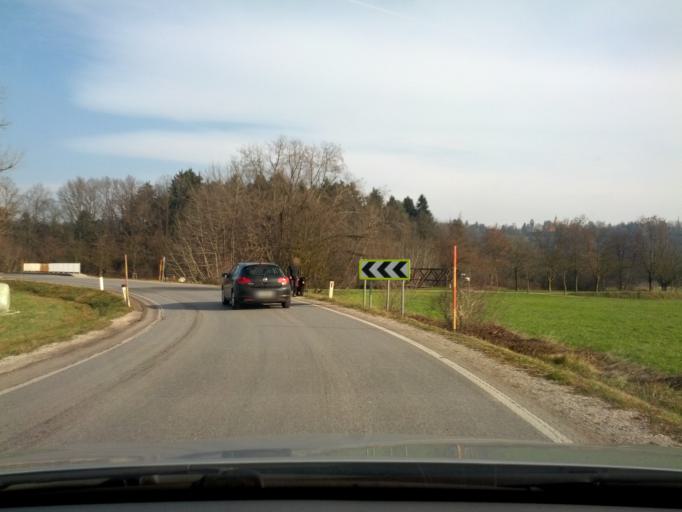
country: SI
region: Ljubljana
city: Ljubljana
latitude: 46.0521
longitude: 14.4609
